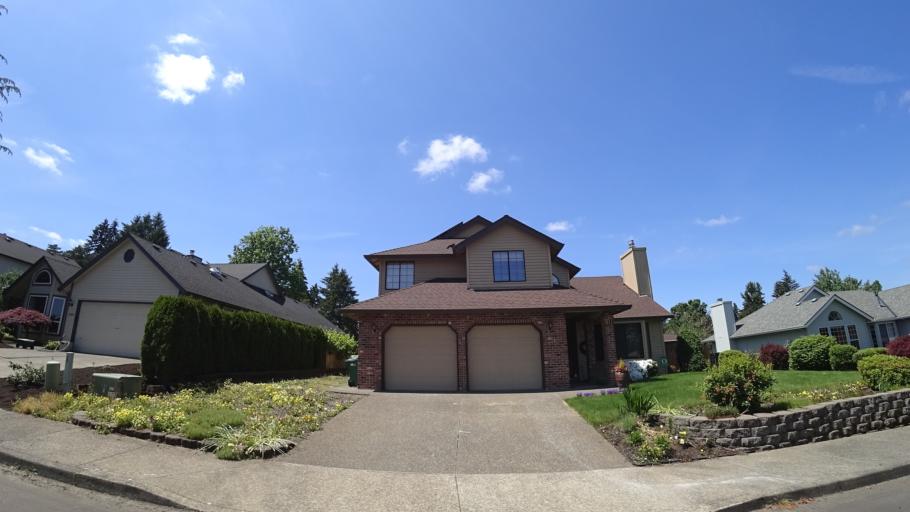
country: US
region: Oregon
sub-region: Washington County
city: Tigard
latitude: 45.4412
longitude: -122.7979
